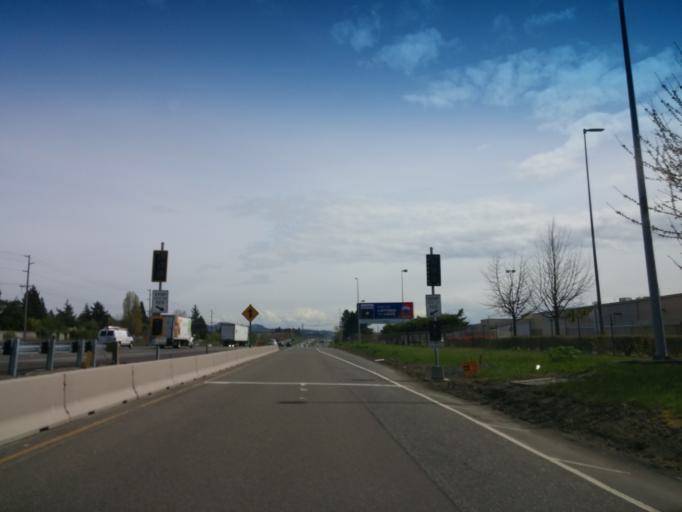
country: US
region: Oregon
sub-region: Washington County
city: Rockcreek
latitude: 45.5399
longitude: -122.8633
